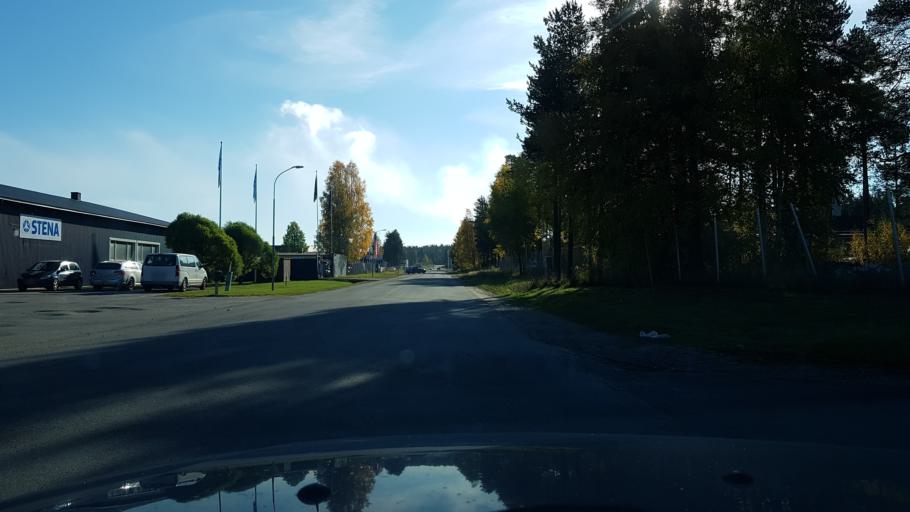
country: SE
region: Norrbotten
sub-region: Pitea Kommun
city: Bergsviken
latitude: 65.3355
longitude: 21.4175
